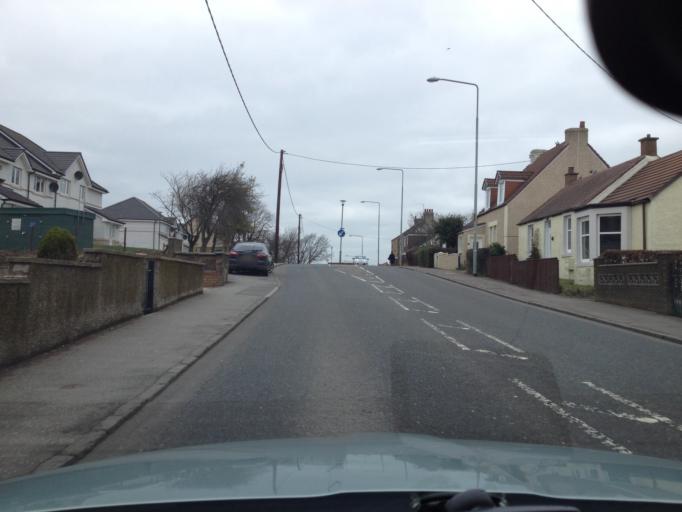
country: GB
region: Scotland
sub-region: West Lothian
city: Livingston
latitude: 55.9150
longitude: -3.5014
